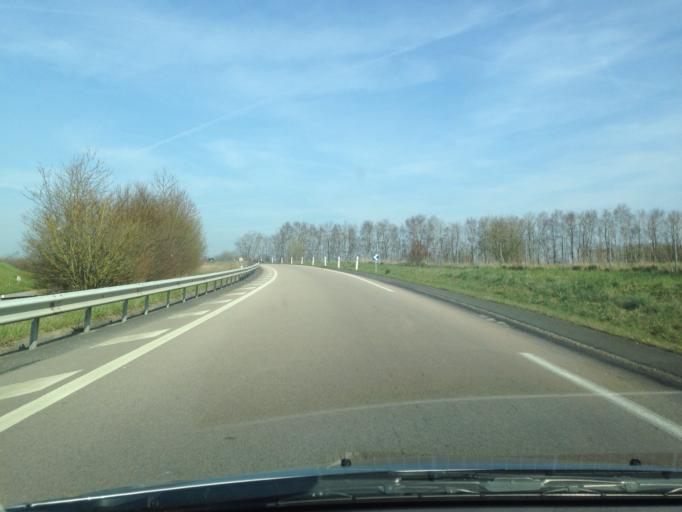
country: FR
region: Haute-Normandie
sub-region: Departement de la Seine-Maritime
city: Saint-Saens
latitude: 49.6493
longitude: 1.2630
